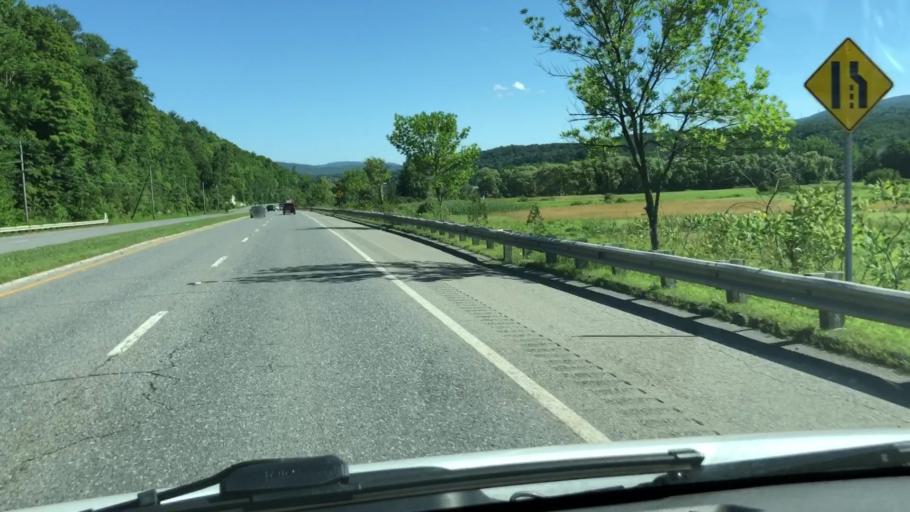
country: US
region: Massachusetts
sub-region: Berkshire County
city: North Adams
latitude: 42.6727
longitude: -73.1072
